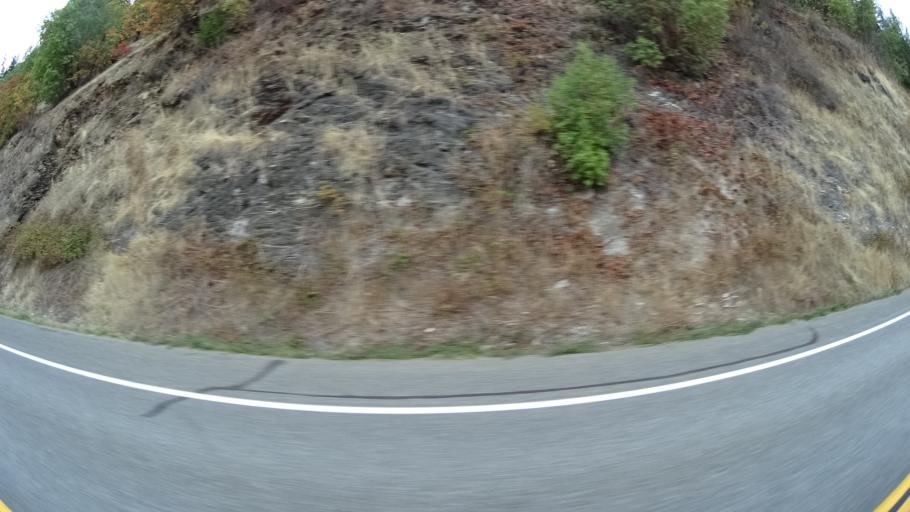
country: US
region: California
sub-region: Siskiyou County
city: Happy Camp
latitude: 41.8105
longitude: -123.3609
